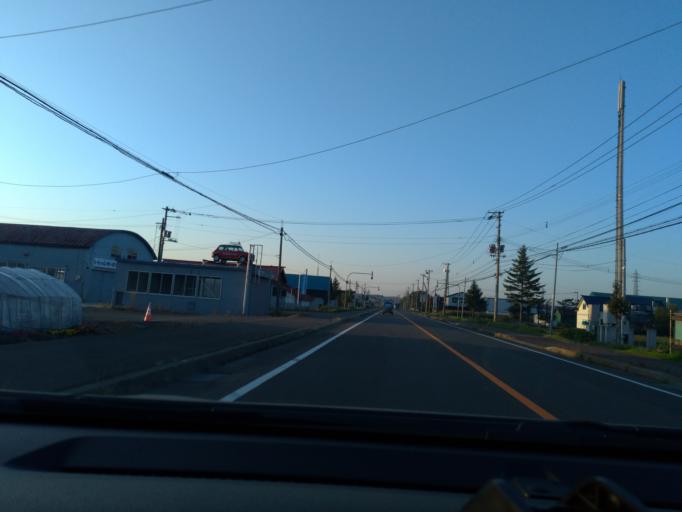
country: JP
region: Hokkaido
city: Tobetsu
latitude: 43.2054
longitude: 141.5202
